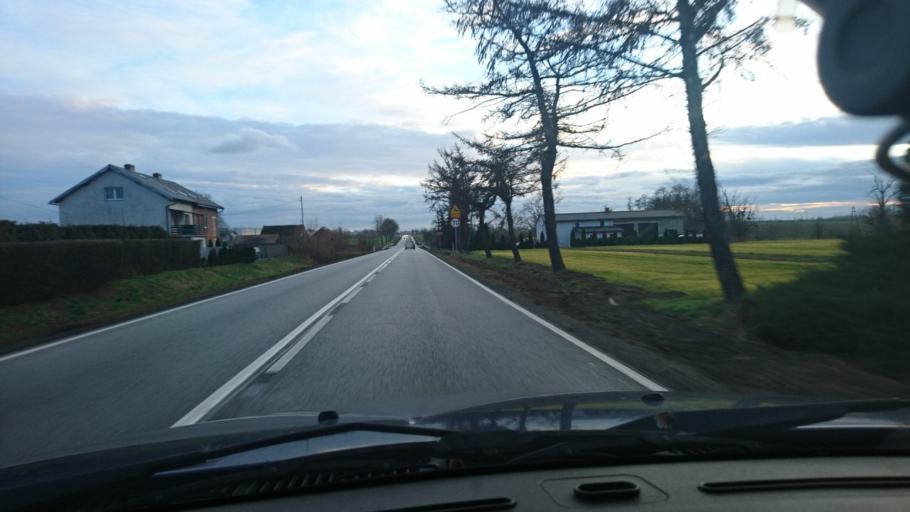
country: PL
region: Opole Voivodeship
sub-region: Powiat kluczborski
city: Kluczbork
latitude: 51.0081
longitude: 18.2045
